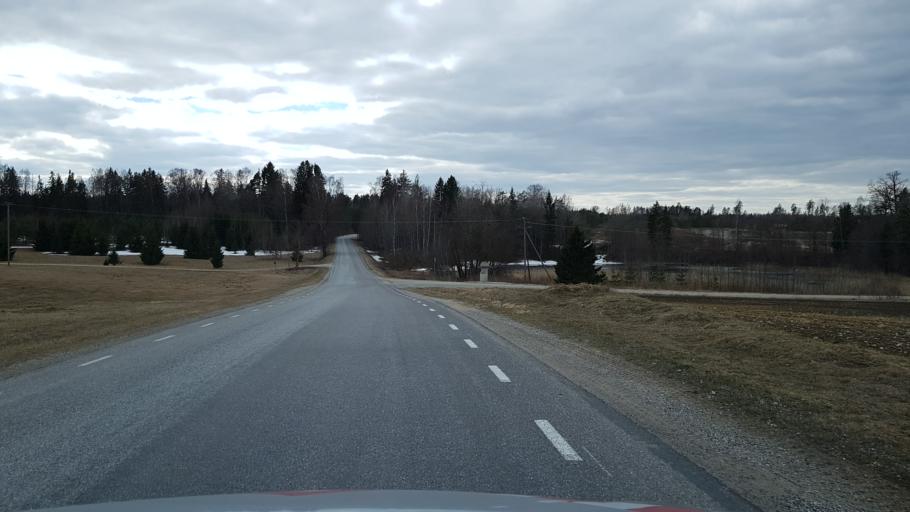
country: EE
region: Laeaene-Virumaa
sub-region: Kadrina vald
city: Kadrina
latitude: 59.2433
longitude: 26.1891
